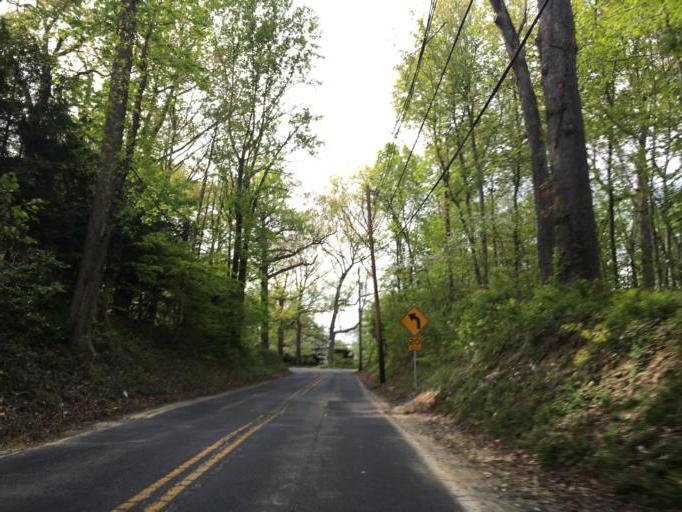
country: US
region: Maryland
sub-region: Howard County
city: Elkridge
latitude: 39.2181
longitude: -76.7203
